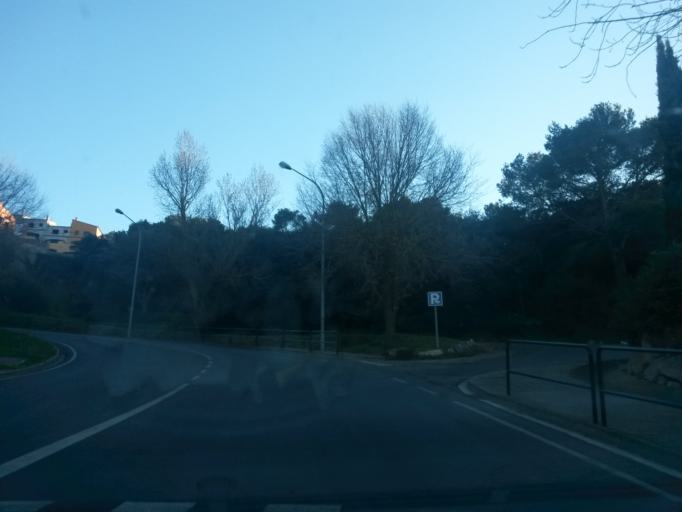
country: ES
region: Catalonia
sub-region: Provincia de Girona
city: Begur
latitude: 41.9534
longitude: 3.2022
